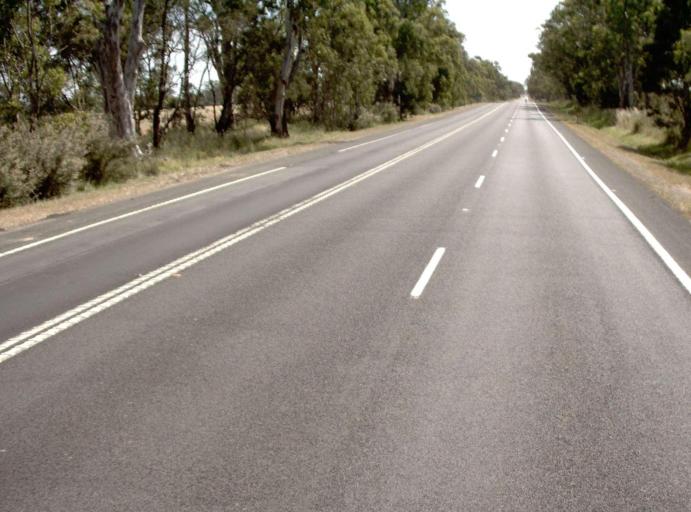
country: AU
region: Victoria
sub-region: Wellington
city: Sale
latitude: -37.9317
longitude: 147.1906
